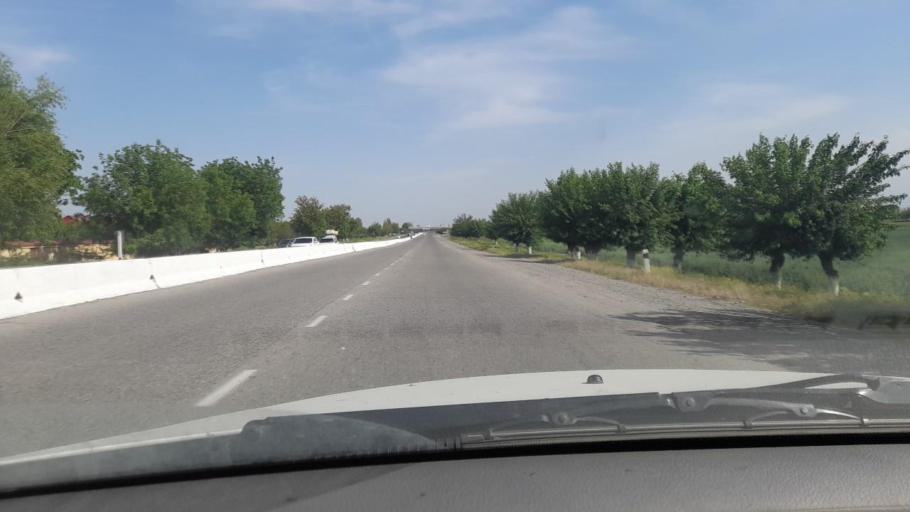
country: UZ
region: Samarqand
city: Daxbet
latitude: 39.7767
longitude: 66.8906
